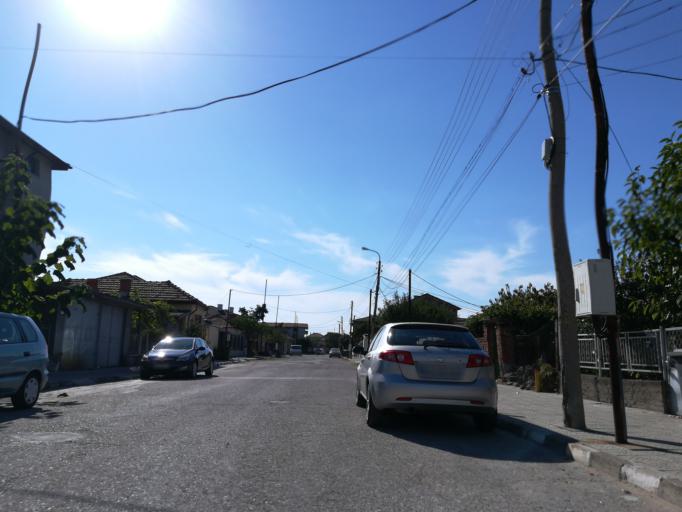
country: BG
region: Stara Zagora
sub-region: Obshtina Chirpan
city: Chirpan
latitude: 42.0931
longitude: 25.2236
